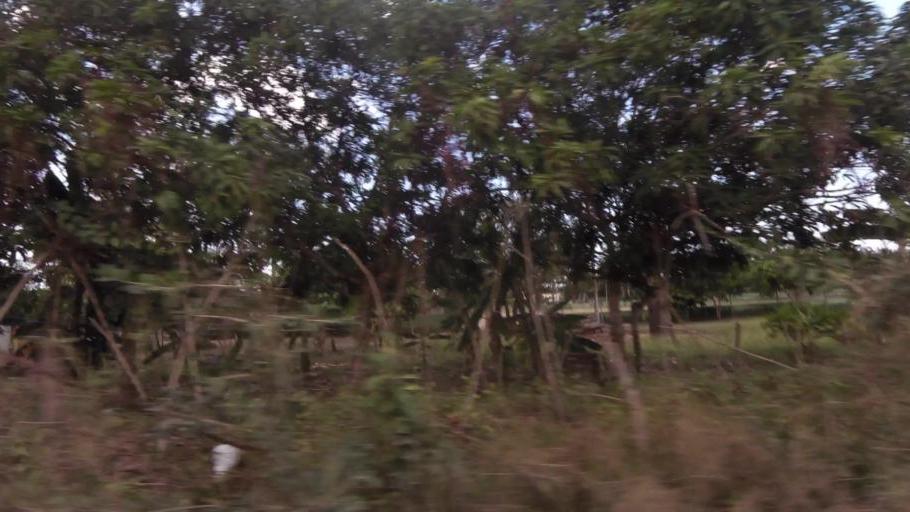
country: CO
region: Bolivar
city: Cartagena
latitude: 10.3701
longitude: -75.4600
